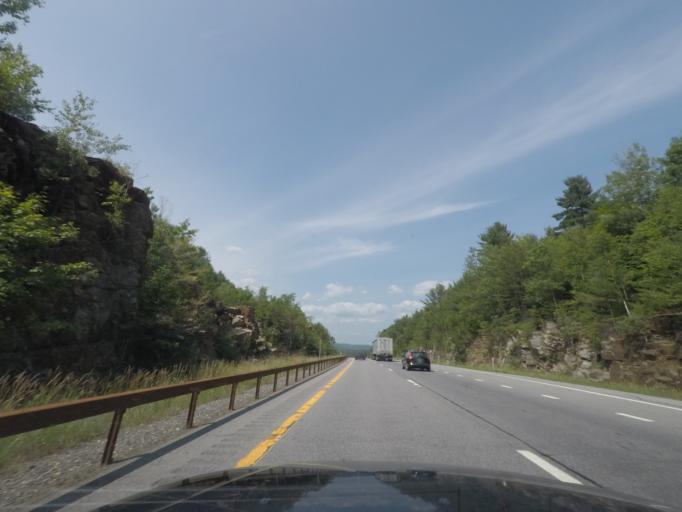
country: US
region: New York
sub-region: Warren County
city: Warrensburg
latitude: 43.7865
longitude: -73.7957
